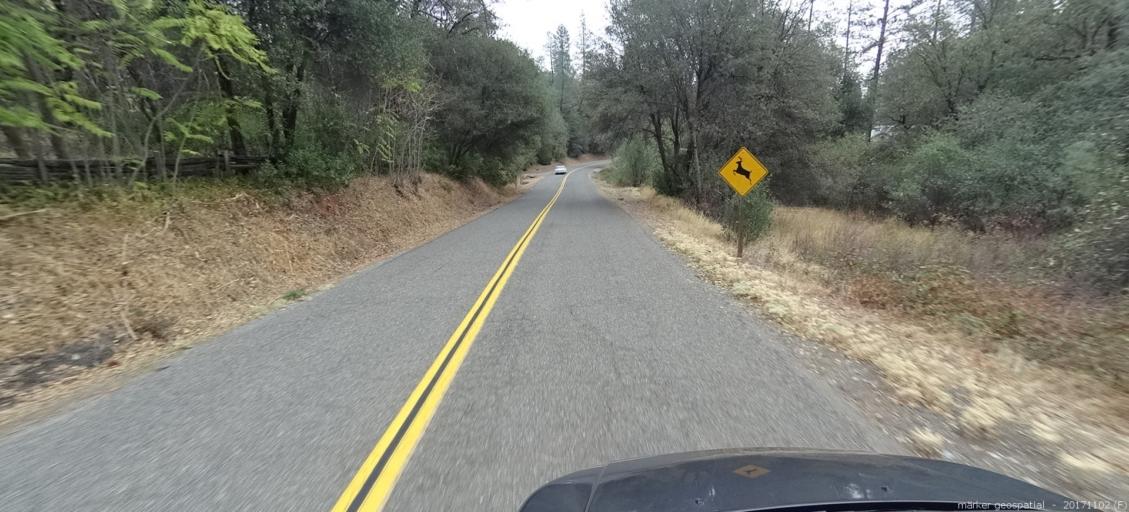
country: US
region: California
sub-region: Shasta County
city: Central Valley (historical)
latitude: 40.6629
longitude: -122.4122
